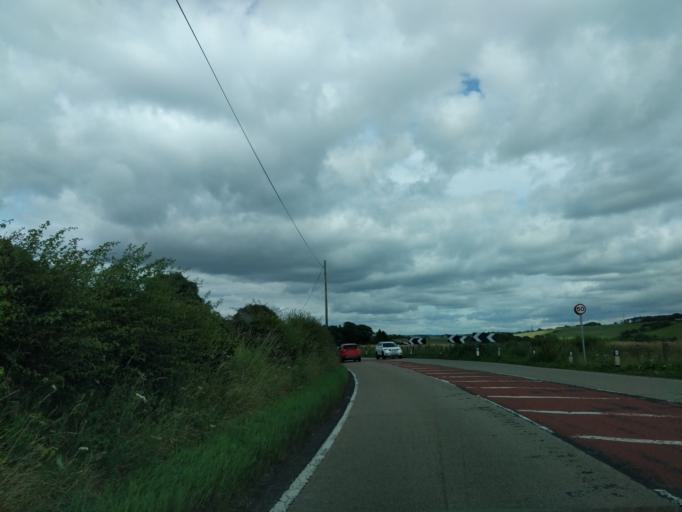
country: GB
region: Scotland
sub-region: South Lanarkshire
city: Strathaven
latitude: 55.6785
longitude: -4.0454
